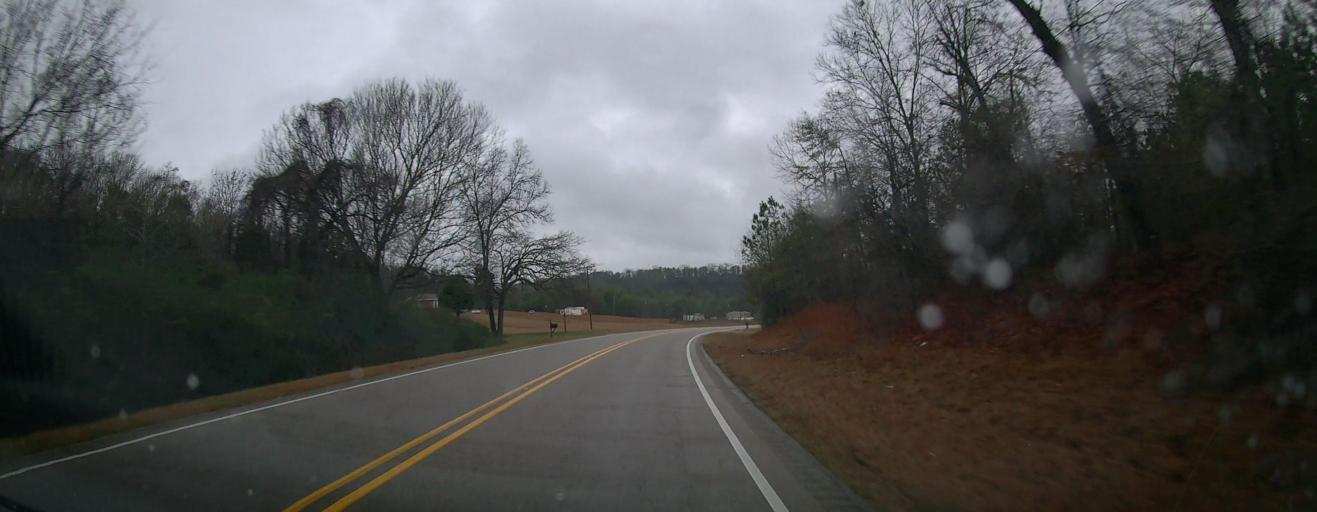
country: US
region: Alabama
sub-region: Autauga County
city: Pine Level
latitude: 32.5228
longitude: -86.6240
